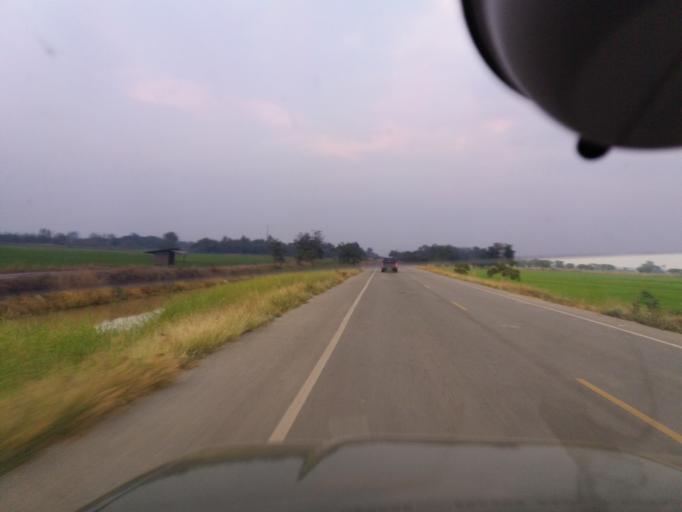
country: TH
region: Suphan Buri
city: Doem Bang Nang Buat
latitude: 14.8939
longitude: 100.1322
